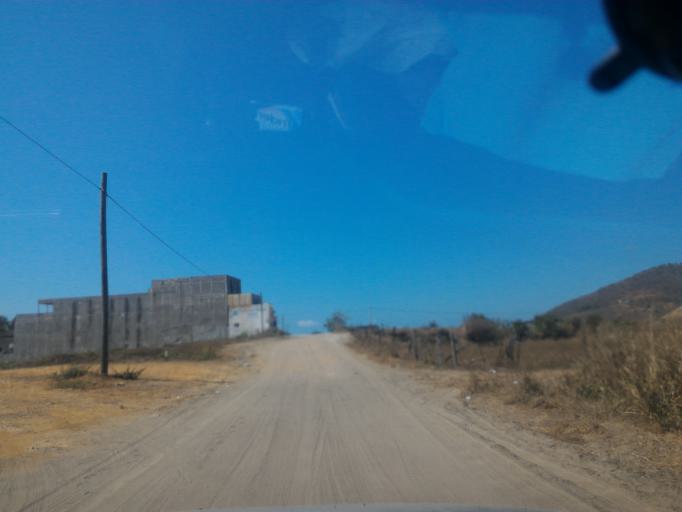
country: MX
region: Michoacan
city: Coahuayana Viejo
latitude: 18.5878
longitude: -103.6813
